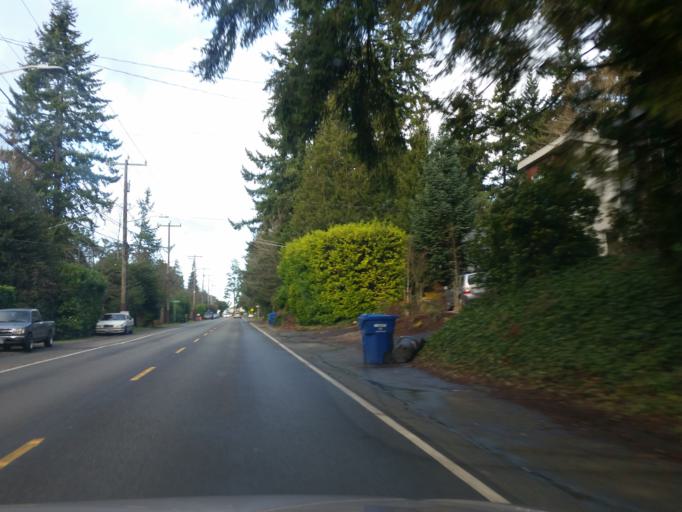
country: US
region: Washington
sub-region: King County
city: Inglewood-Finn Hill
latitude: 47.7002
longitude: -122.2777
